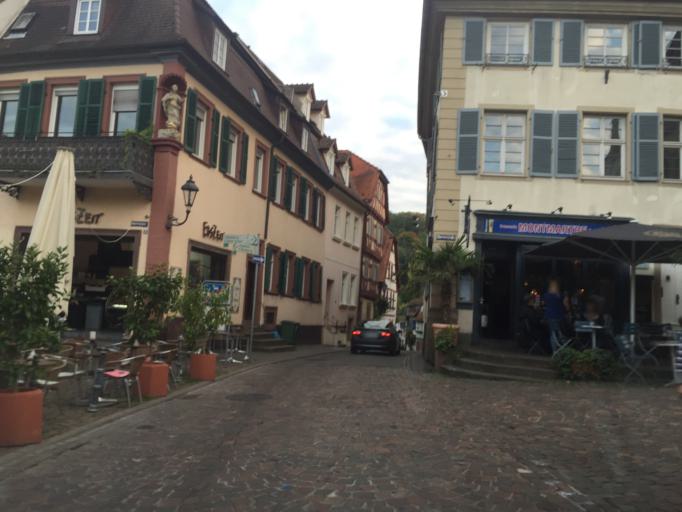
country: DE
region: Baden-Wuerttemberg
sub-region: Karlsruhe Region
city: Weinheim
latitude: 49.5464
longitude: 8.6717
